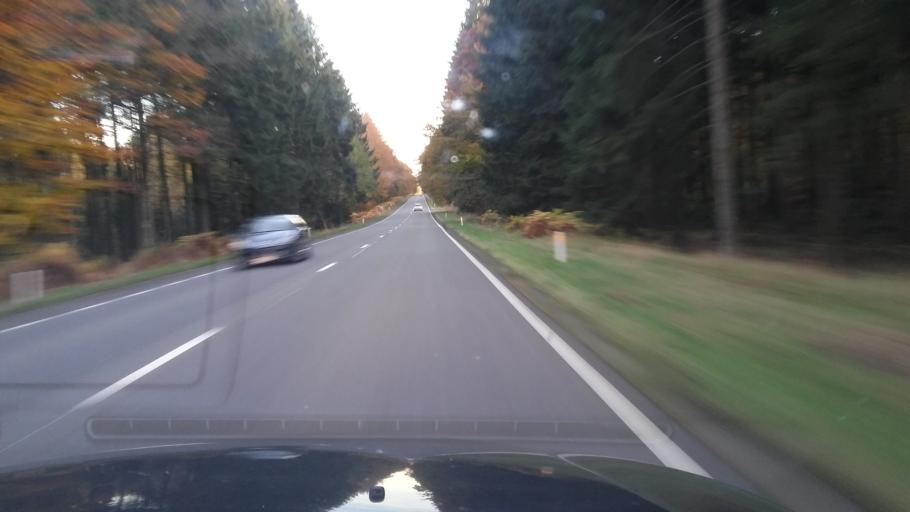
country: BE
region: Wallonia
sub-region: Province du Luxembourg
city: Herbeumont
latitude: 49.7453
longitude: 5.2152
